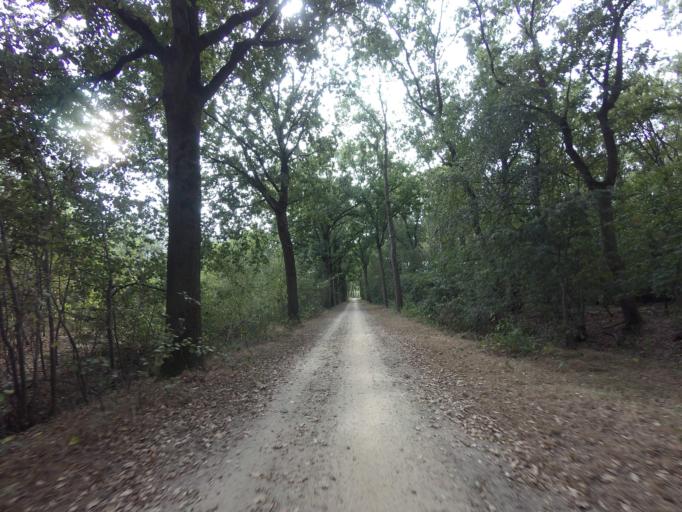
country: NL
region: North Brabant
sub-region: Gemeente Helmond
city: Helmond
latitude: 51.5160
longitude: 5.7606
